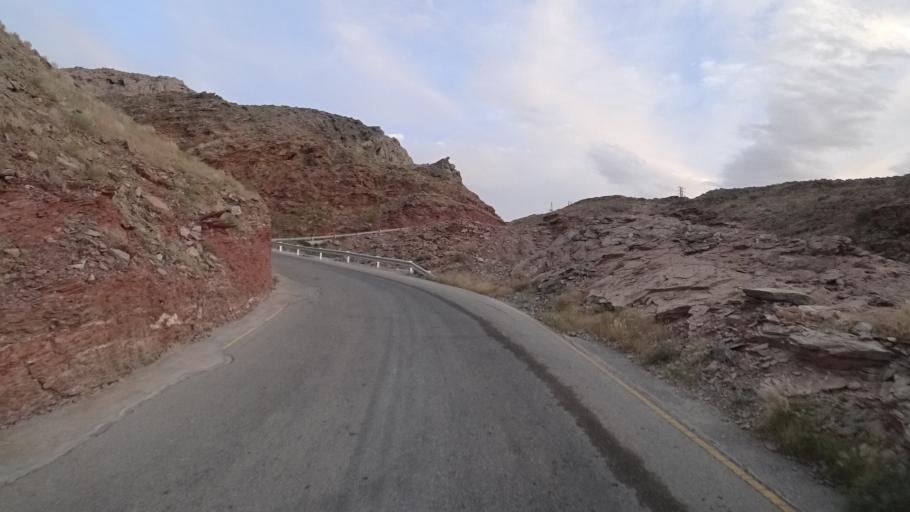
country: OM
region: Muhafazat Masqat
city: Muscat
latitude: 23.5749
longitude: 58.5497
